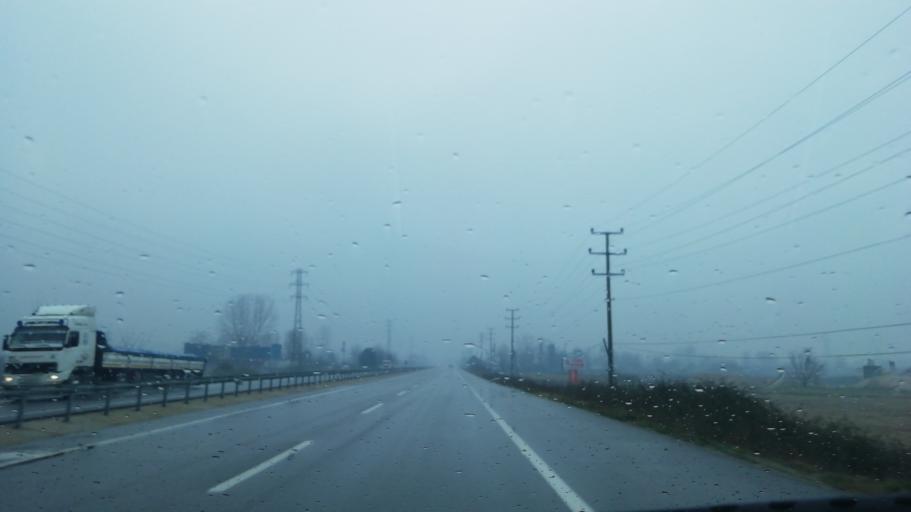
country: TR
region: Sakarya
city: Akyazi
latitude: 40.6398
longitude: 30.6162
